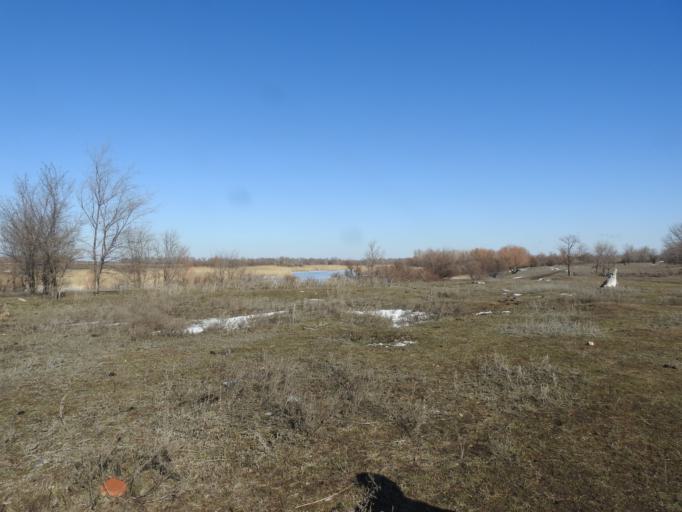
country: RU
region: Saratov
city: Yershov
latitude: 51.3734
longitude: 48.2422
